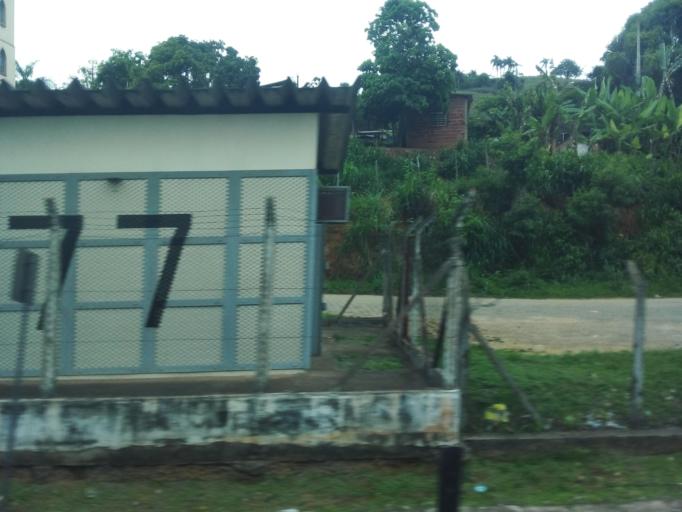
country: BR
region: Minas Gerais
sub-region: Nova Era
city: Nova Era
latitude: -19.7407
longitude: -43.0180
